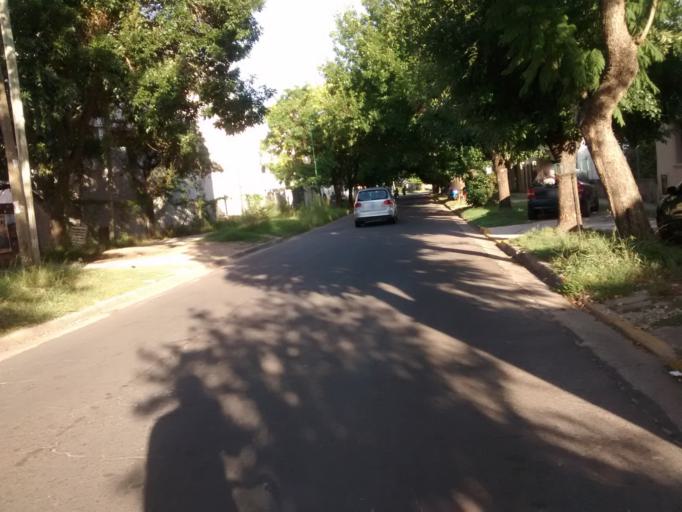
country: AR
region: Buenos Aires
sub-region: Partido de La Plata
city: La Plata
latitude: -34.9130
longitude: -57.9265
